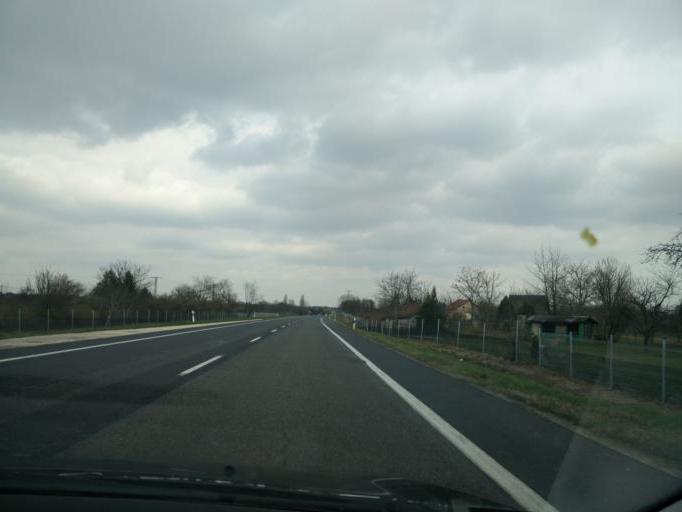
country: HU
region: Gyor-Moson-Sopron
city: Toltestava
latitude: 47.7155
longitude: 17.7238
